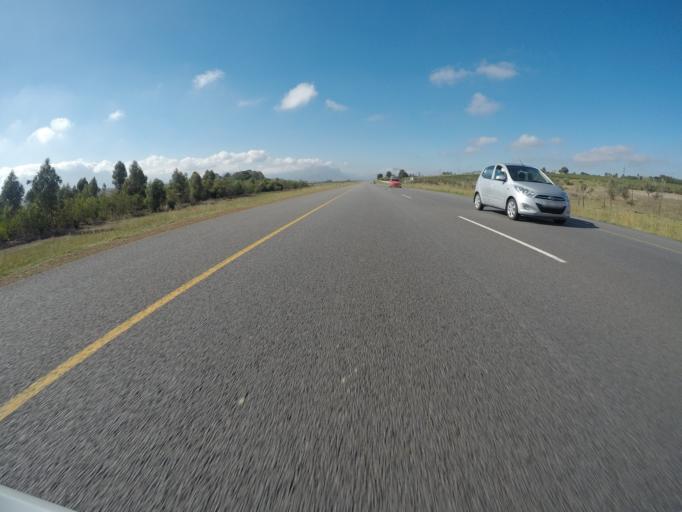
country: ZA
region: Western Cape
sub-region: City of Cape Town
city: Kraaifontein
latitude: -33.8563
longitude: 18.8085
